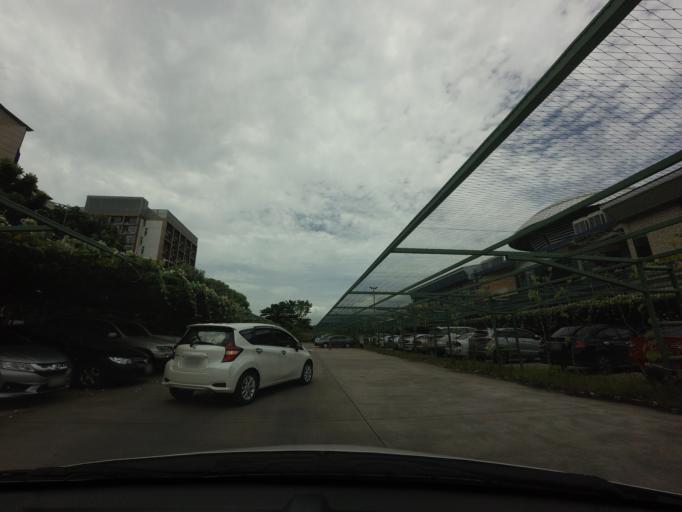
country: TH
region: Bangkok
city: Chatuchak
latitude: 13.8542
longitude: 100.5784
